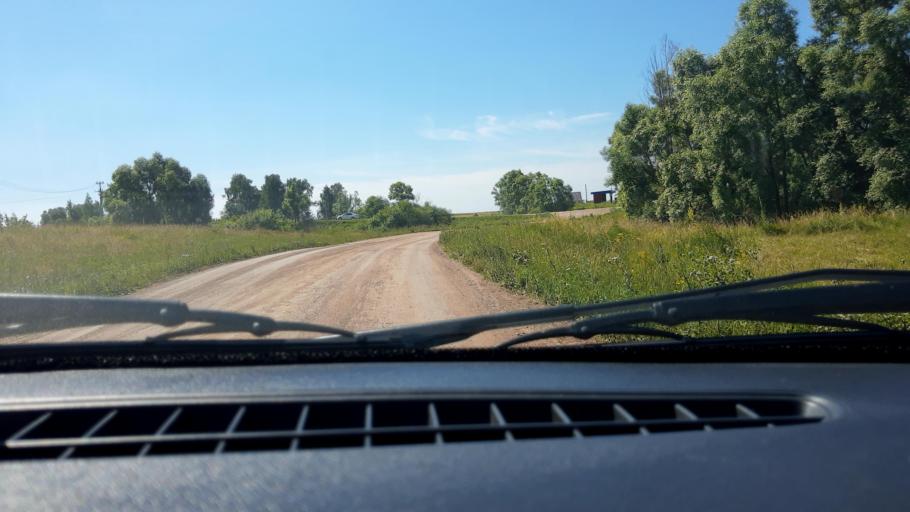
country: RU
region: Bashkortostan
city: Karmaskaly
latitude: 54.3578
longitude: 55.9029
